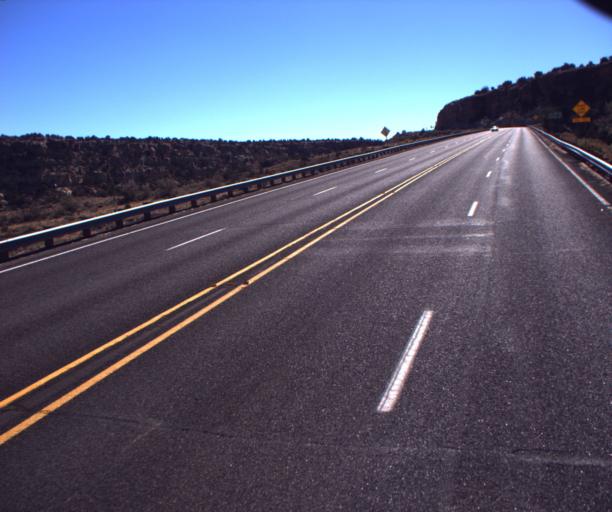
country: US
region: Arizona
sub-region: Navajo County
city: First Mesa
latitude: 35.8114
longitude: -110.2011
